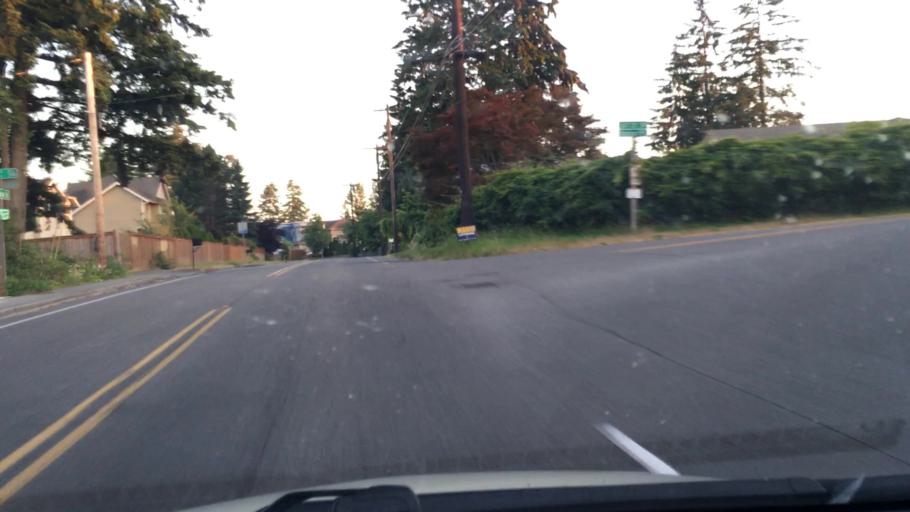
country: US
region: Washington
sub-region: Snohomish County
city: Martha Lake
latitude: 47.8536
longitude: -122.2511
